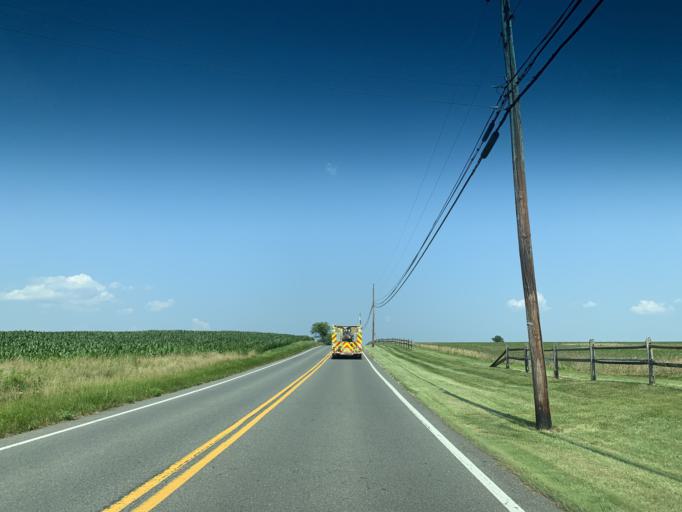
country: US
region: Maryland
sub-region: Montgomery County
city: Poolesville
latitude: 39.1241
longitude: -77.3635
